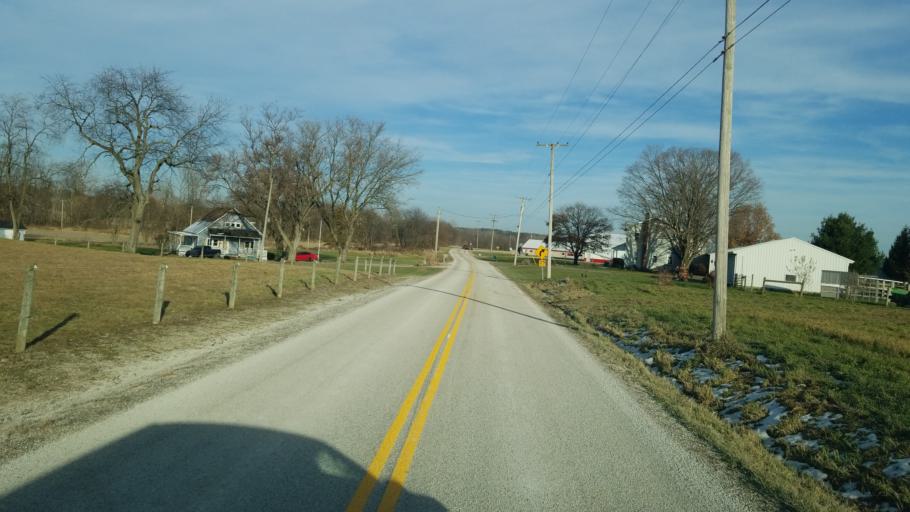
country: US
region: Ohio
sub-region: Ashland County
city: Ashland
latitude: 40.7977
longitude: -82.2367
